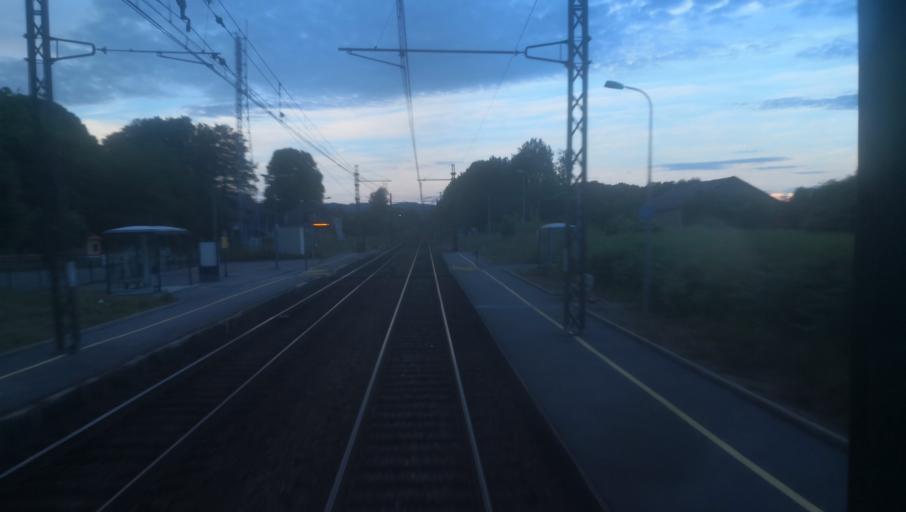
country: FR
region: Limousin
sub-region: Departement de la Haute-Vienne
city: Ambazac
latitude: 45.9938
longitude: 1.4797
